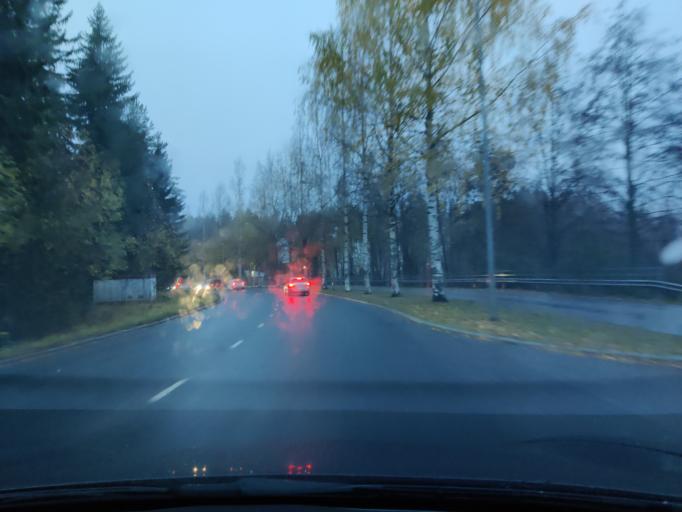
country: FI
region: Northern Savo
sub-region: Kuopio
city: Kuopio
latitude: 62.8446
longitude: 27.6567
